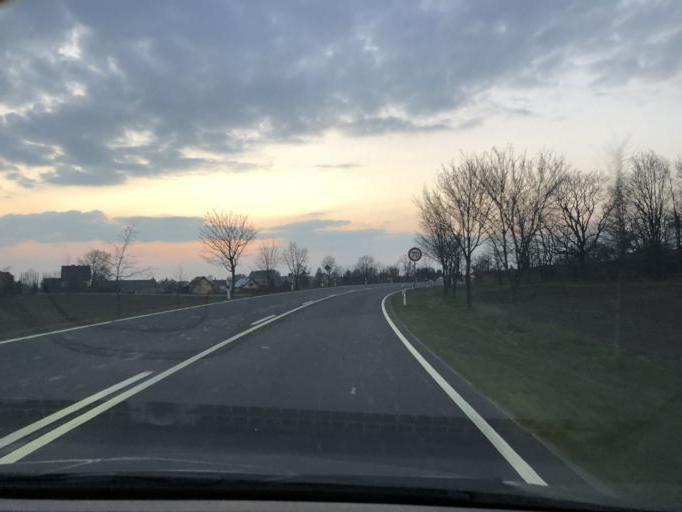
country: DE
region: Saxony
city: Tauscha
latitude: 51.2827
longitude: 13.7995
